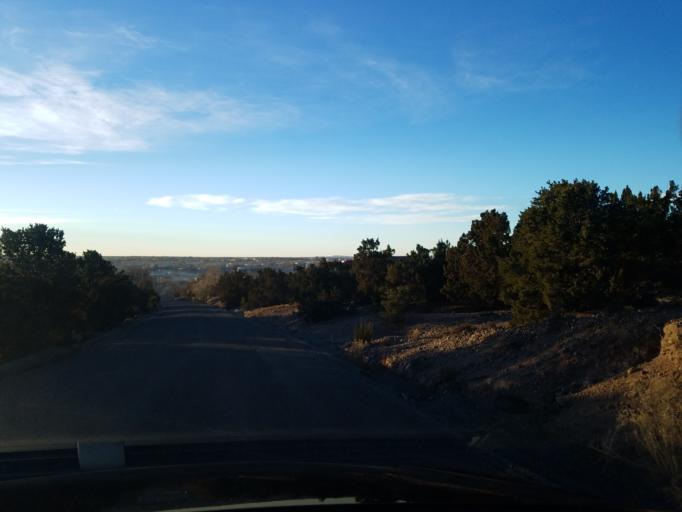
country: US
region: New Mexico
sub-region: Santa Fe County
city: Agua Fria
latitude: 35.6738
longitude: -105.9951
